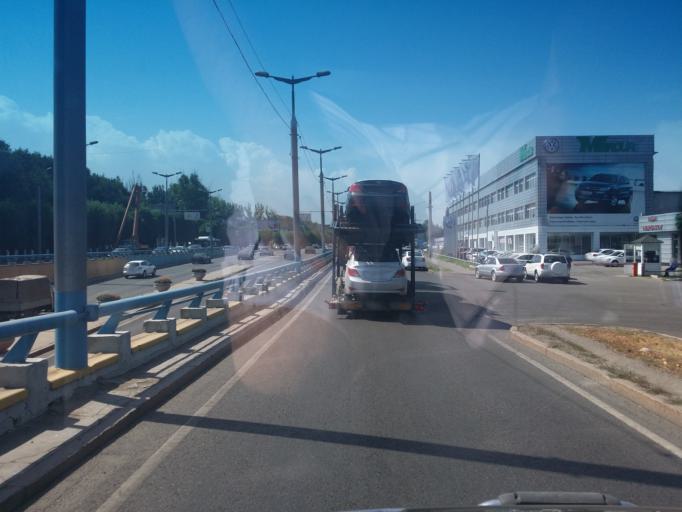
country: KZ
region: Almaty Oblysy
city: Pervomayskiy
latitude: 43.3399
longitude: 76.9834
